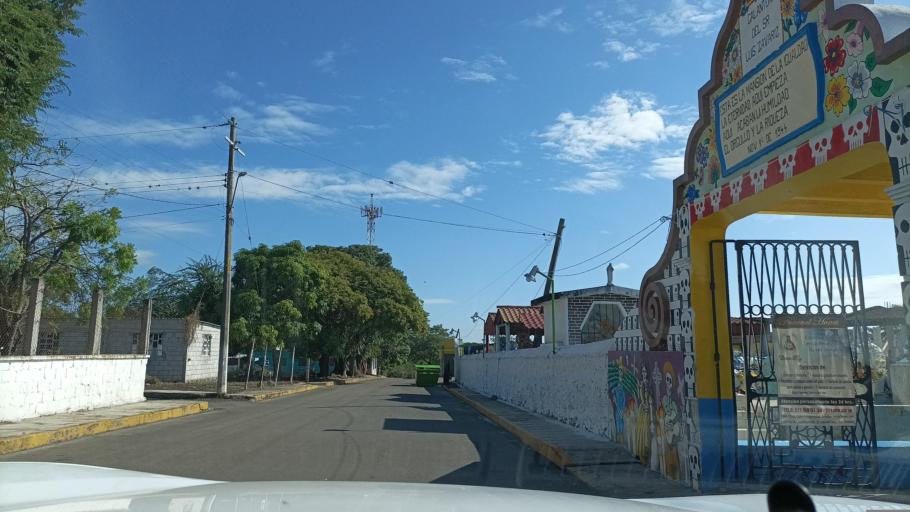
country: MX
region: Veracruz
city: Paso del Macho
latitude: 18.9670
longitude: -96.7184
